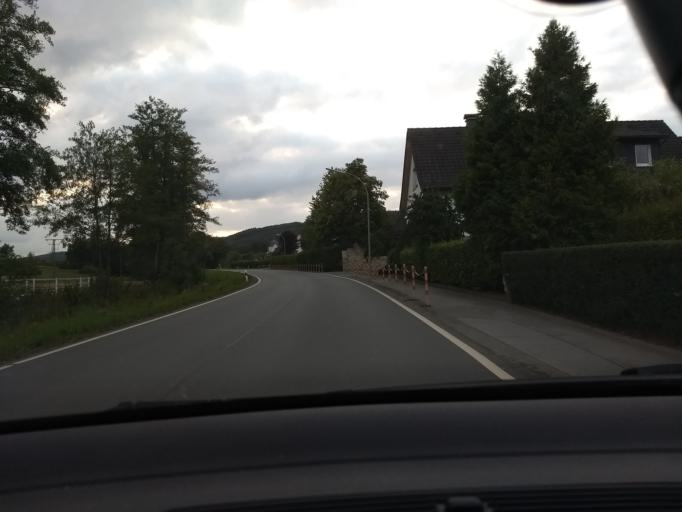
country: DE
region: North Rhine-Westphalia
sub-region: Regierungsbezirk Arnsberg
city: Arnsberg
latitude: 51.3558
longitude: 8.1624
